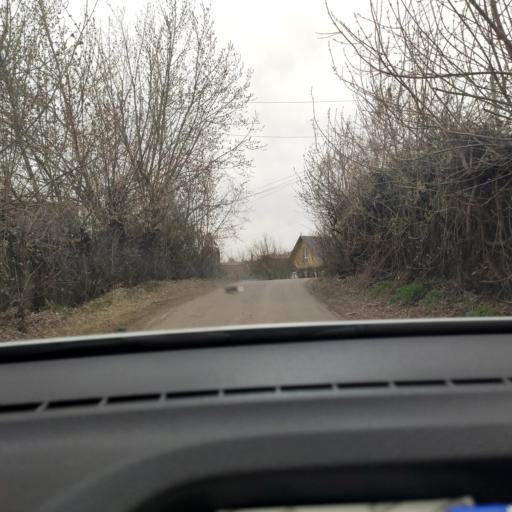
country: RU
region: Bashkortostan
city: Avdon
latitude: 54.6235
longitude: 55.5983
